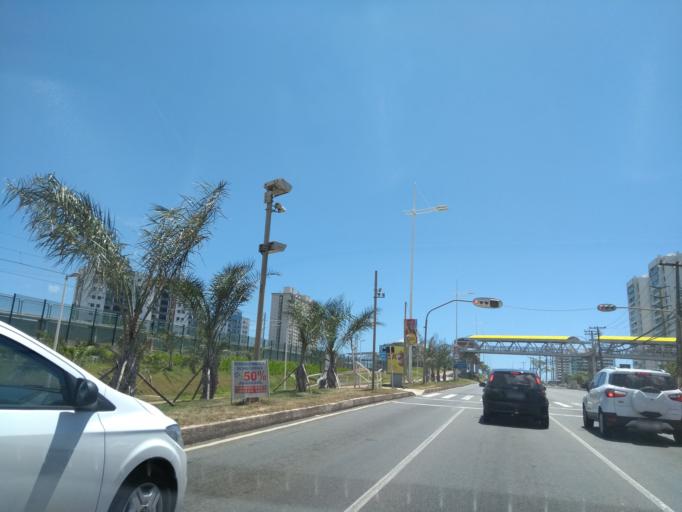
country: BR
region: Bahia
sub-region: Lauro De Freitas
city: Lauro de Freitas
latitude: -12.9387
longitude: -38.4085
